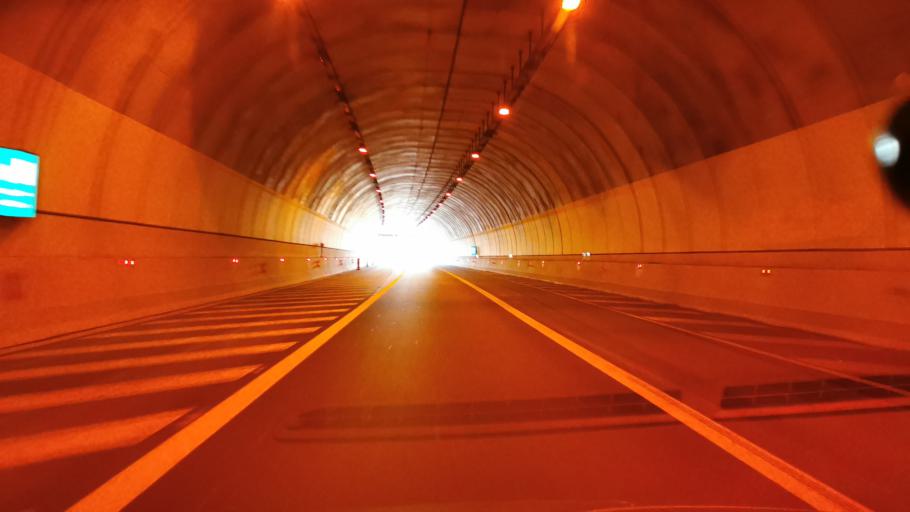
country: IT
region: Piedmont
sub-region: Provincia di Cuneo
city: Cuneo
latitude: 44.4284
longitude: 7.5658
